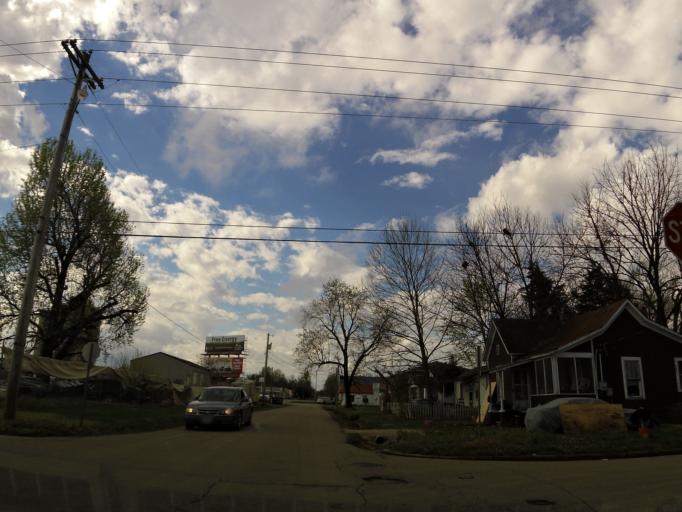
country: US
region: Missouri
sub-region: Butler County
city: Poplar Bluff
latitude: 36.7581
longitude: -90.3857
